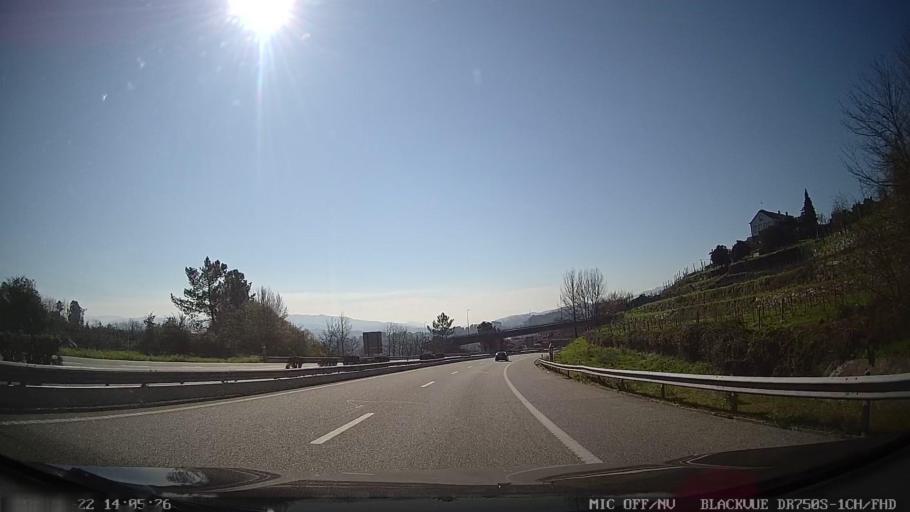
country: PT
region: Porto
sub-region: Marco de Canaveses
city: Marco de Canavezes
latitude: 41.2218
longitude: -8.1481
